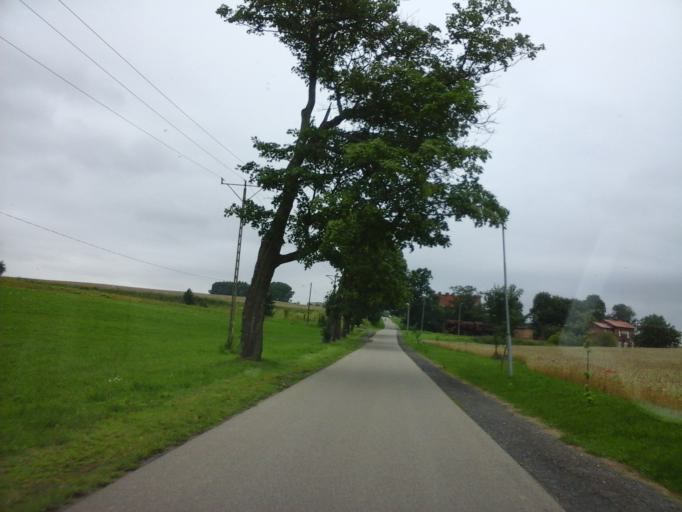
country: PL
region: West Pomeranian Voivodeship
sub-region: Powiat choszczenski
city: Pelczyce
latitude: 53.1018
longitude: 15.3345
